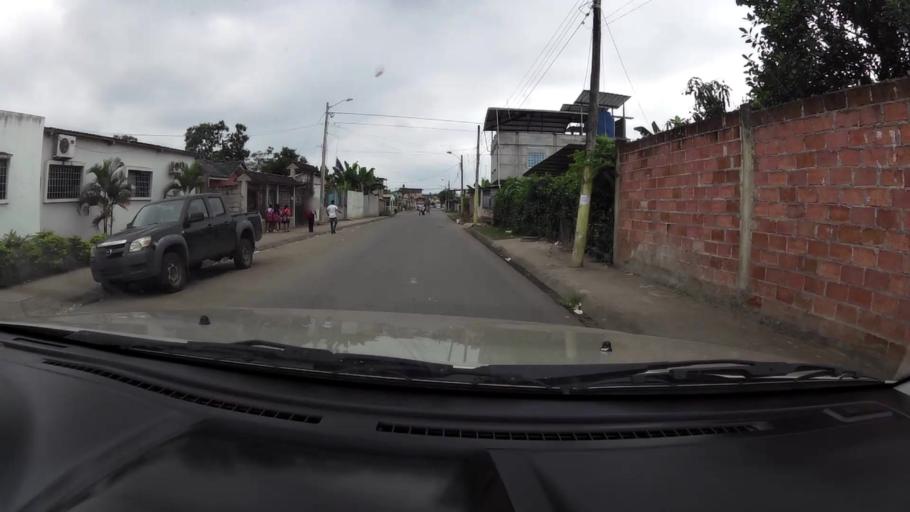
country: EC
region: El Oro
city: Pasaje
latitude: -3.2375
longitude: -79.8282
